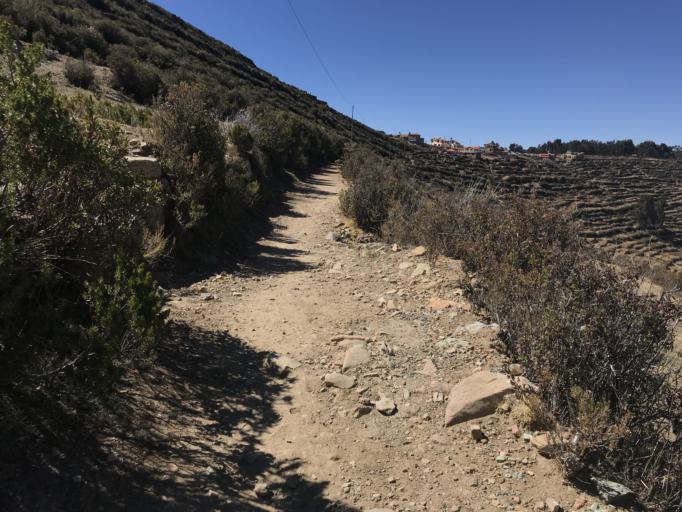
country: BO
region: La Paz
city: Yumani
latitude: -16.0334
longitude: -69.1549
